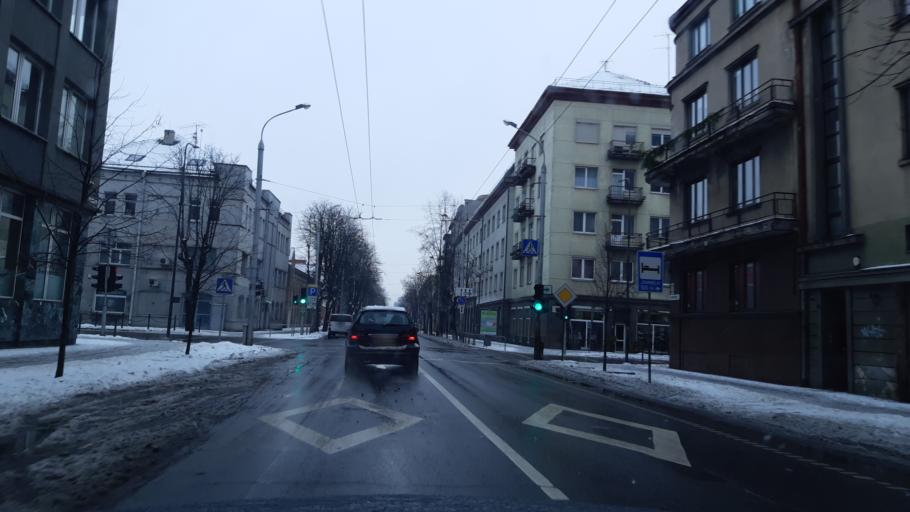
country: LT
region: Kauno apskritis
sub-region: Kaunas
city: Kaunas
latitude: 54.8955
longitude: 23.9181
